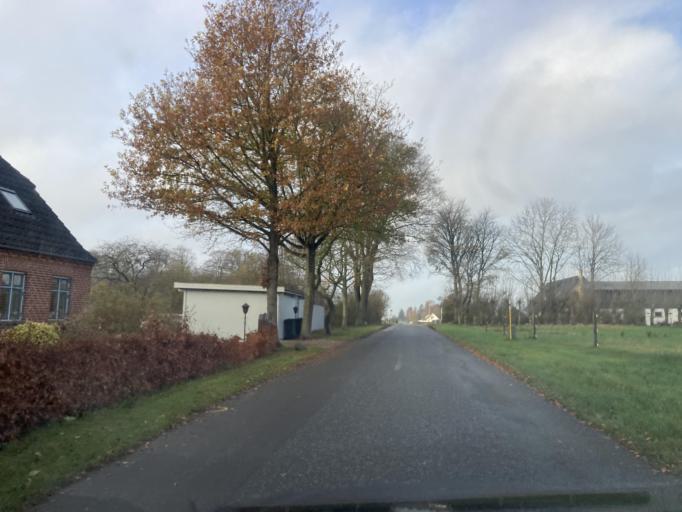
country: DK
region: Zealand
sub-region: Lolland Kommune
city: Rodby
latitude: 54.7923
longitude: 11.3574
